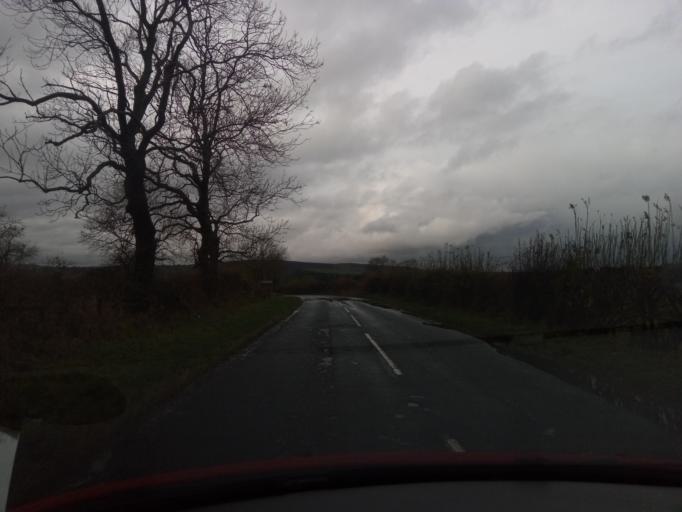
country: GB
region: England
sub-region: County Durham
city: Muggleswick
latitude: 54.8559
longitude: -1.9416
